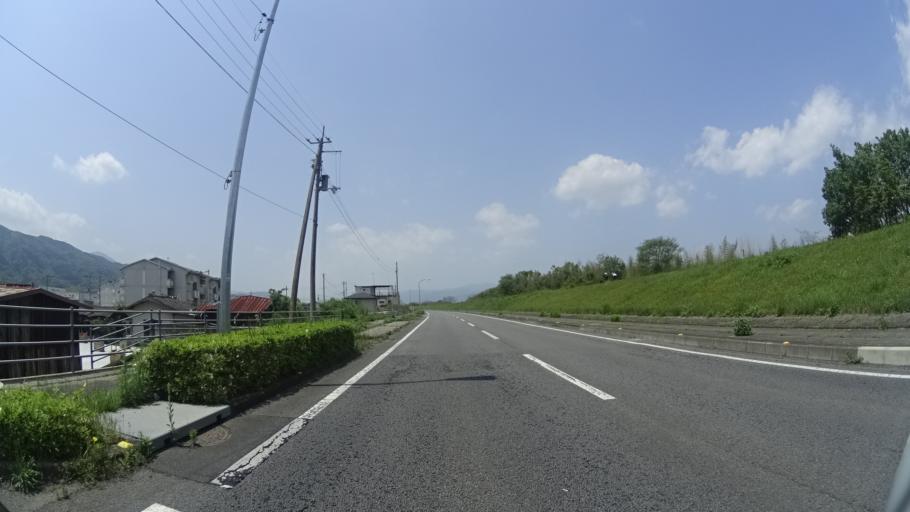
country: JP
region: Tokushima
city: Kamojimacho-jogejima
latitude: 34.0619
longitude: 134.2926
